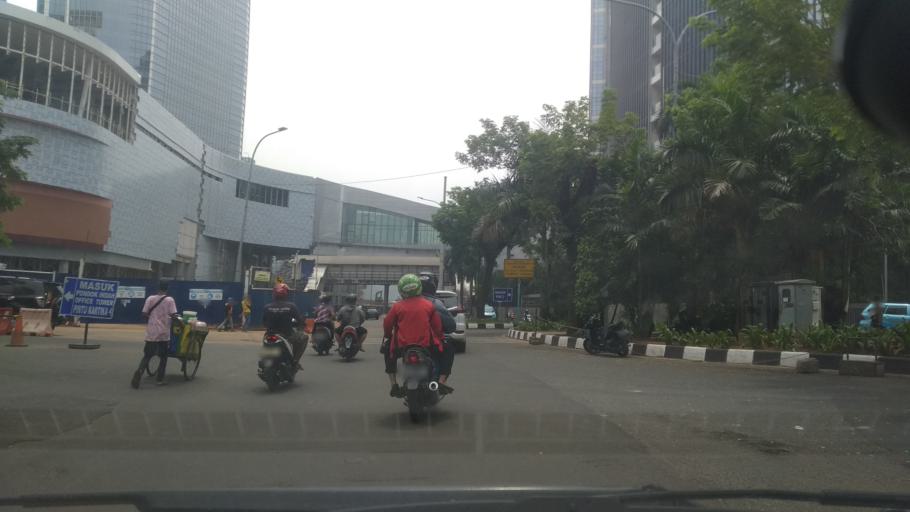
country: ID
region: Banten
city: South Tangerang
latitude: -6.2652
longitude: 106.7816
